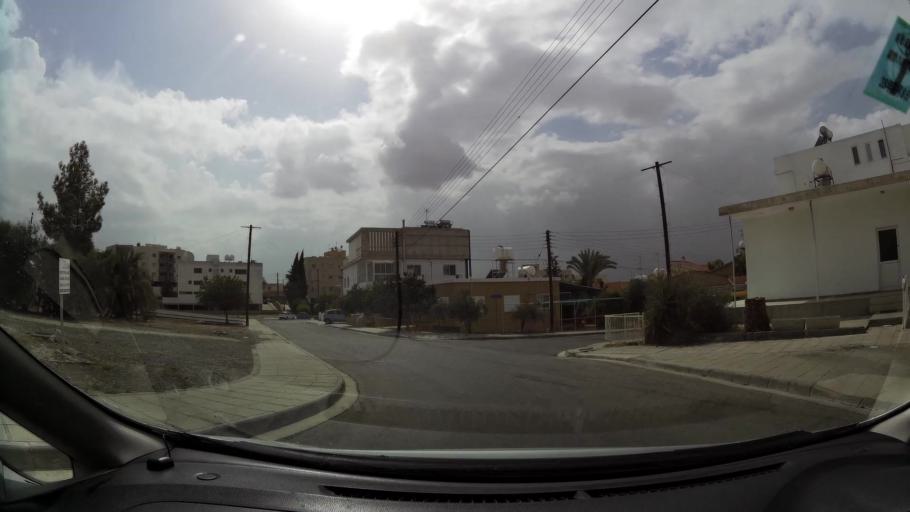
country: CY
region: Lefkosia
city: Geri
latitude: 35.1073
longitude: 33.3775
